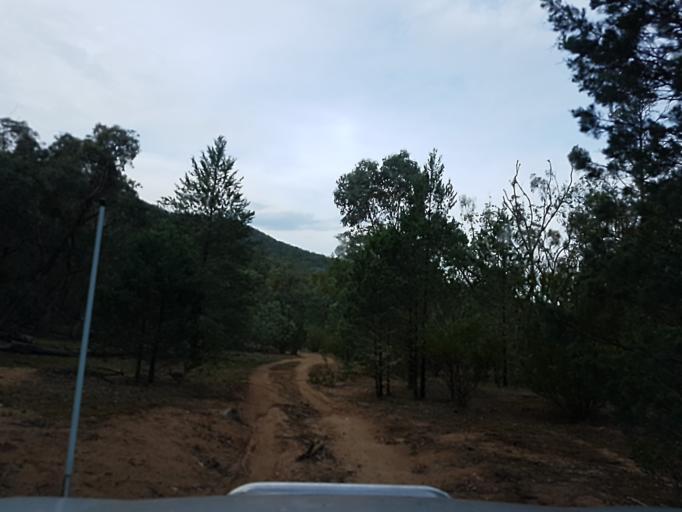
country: AU
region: New South Wales
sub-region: Snowy River
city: Jindabyne
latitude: -36.9450
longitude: 148.3830
